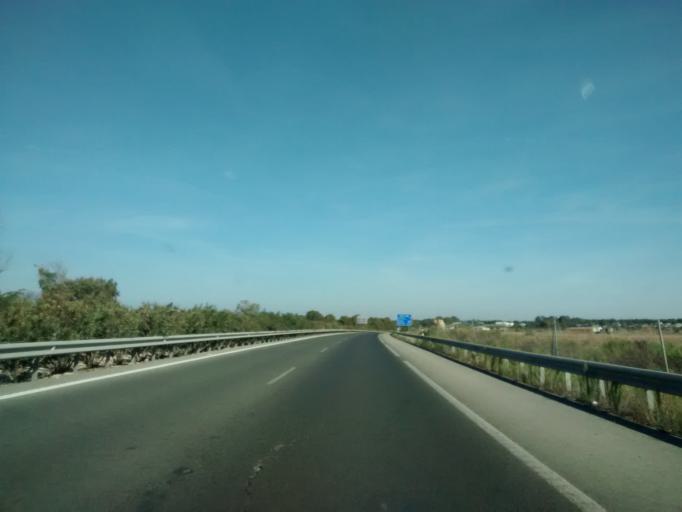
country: ES
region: Andalusia
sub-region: Provincia de Cadiz
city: Chiclana de la Frontera
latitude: 36.3619
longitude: -6.1101
